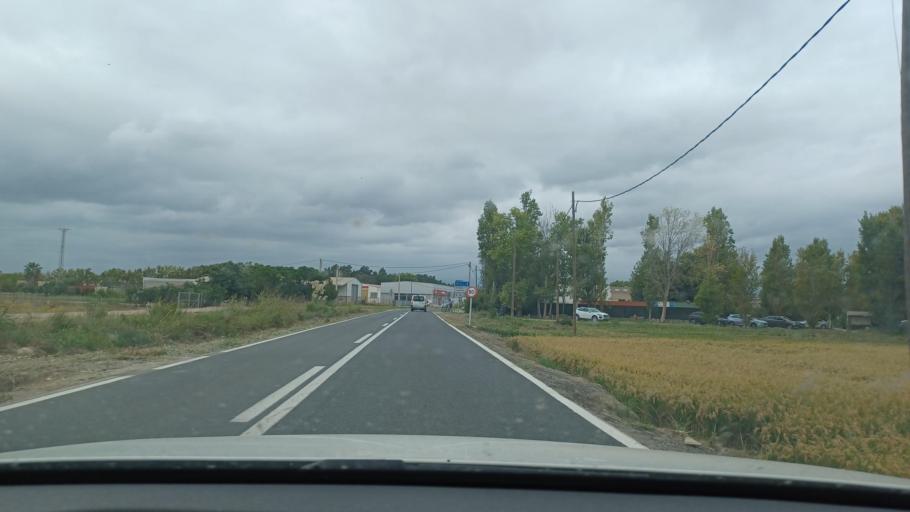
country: ES
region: Catalonia
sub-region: Provincia de Tarragona
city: Amposta
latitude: 40.7062
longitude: 0.5951
